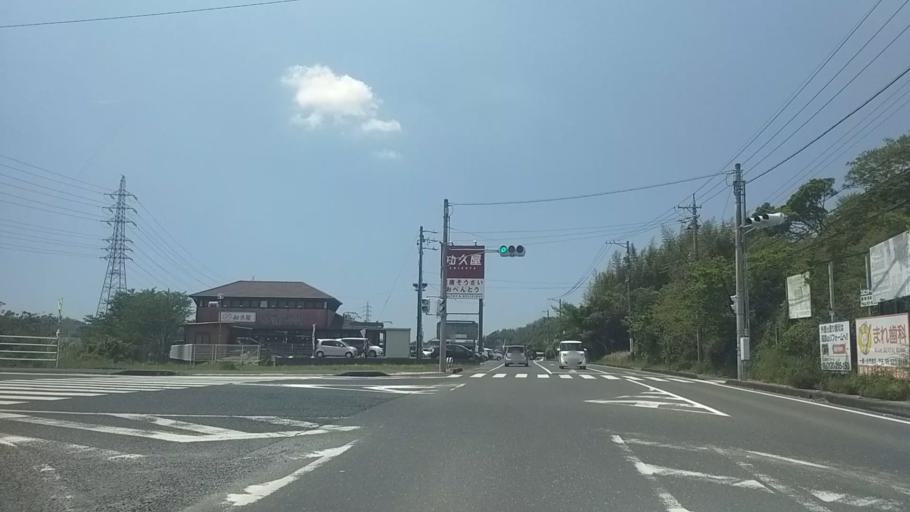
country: JP
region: Shizuoka
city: Hamamatsu
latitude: 34.7711
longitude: 137.6676
